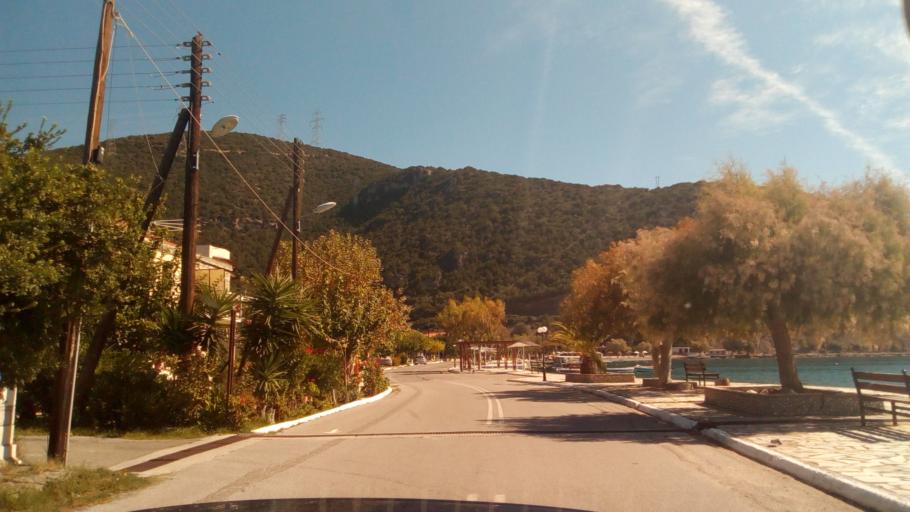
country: GR
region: West Greece
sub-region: Nomos Achaias
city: Selianitika
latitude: 38.3735
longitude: 22.0931
